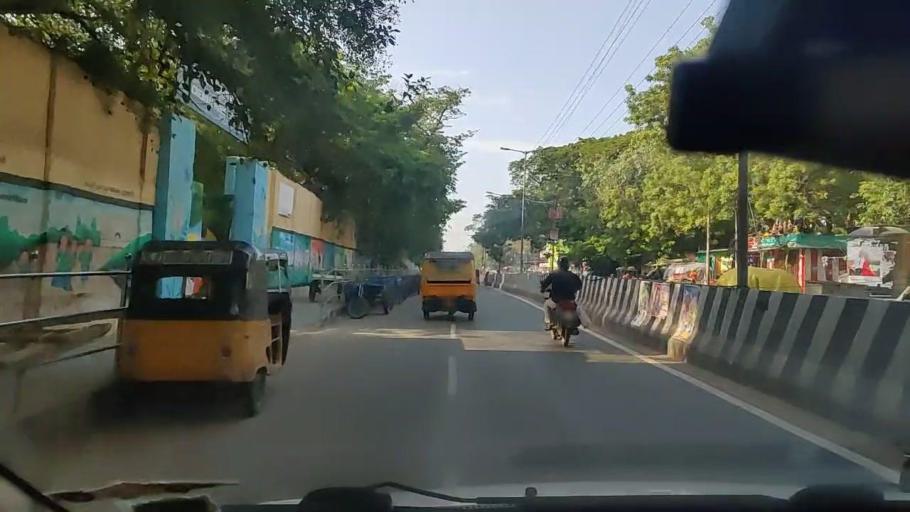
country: IN
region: Tamil Nadu
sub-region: Chennai
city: George Town
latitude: 13.0952
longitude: 80.2752
